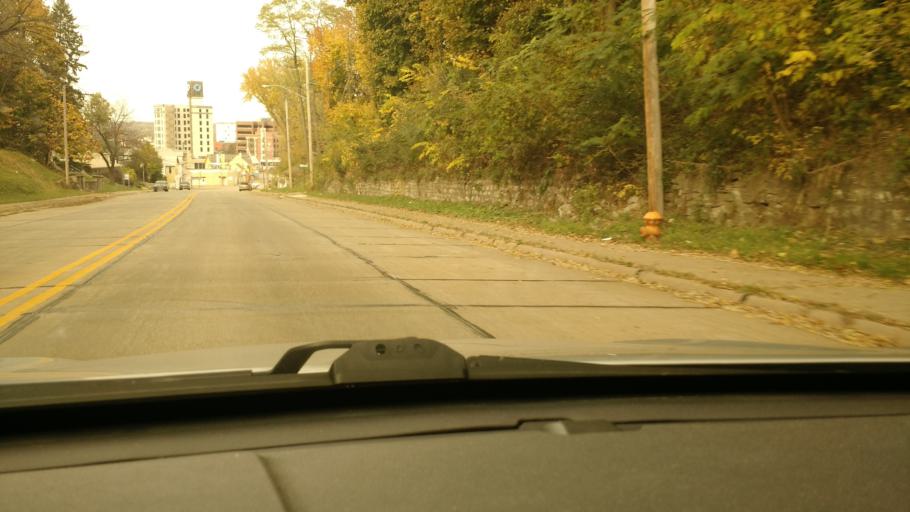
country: US
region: Illinois
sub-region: Rock Island County
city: Moline
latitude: 41.5018
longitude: -90.5156
